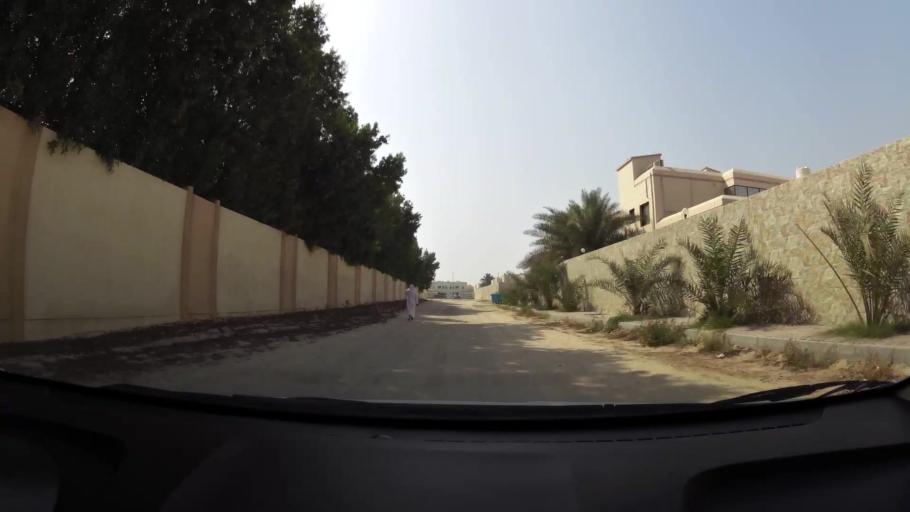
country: AE
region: Ajman
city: Ajman
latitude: 25.3893
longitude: 55.4245
